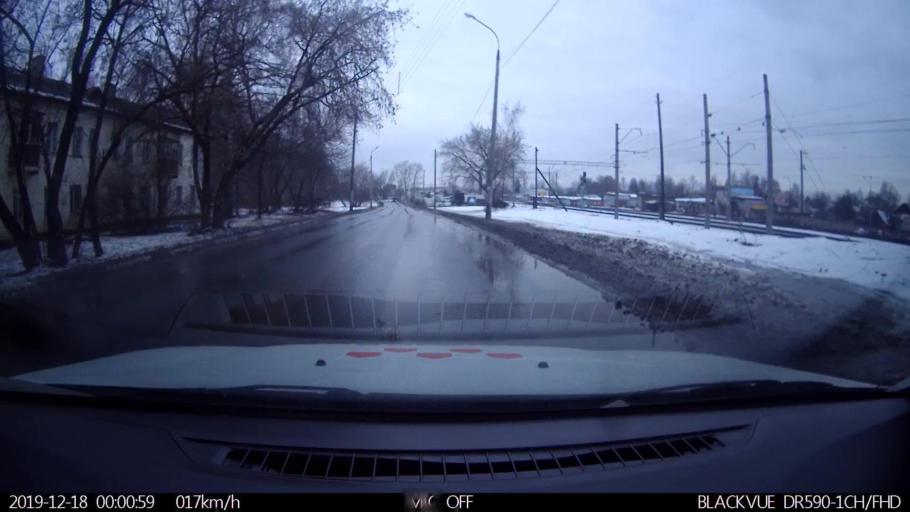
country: RU
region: Nizjnij Novgorod
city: Gorbatovka
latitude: 56.3681
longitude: 43.8269
